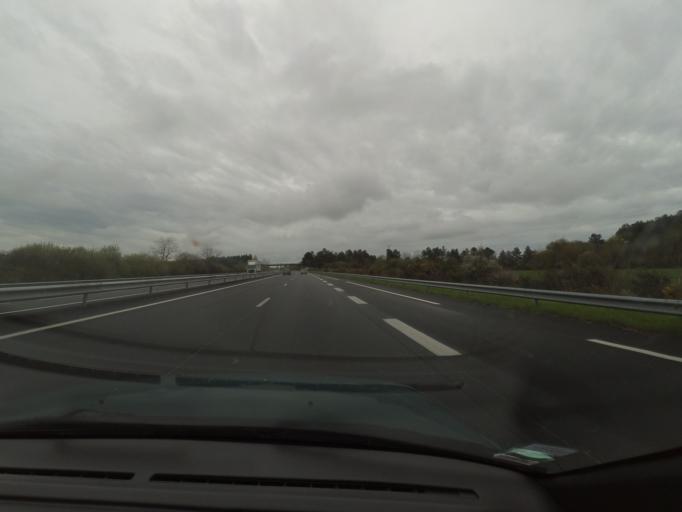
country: FR
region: Pays de la Loire
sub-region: Departement de Maine-et-Loire
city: Durtal
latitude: 47.6281
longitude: -0.2775
